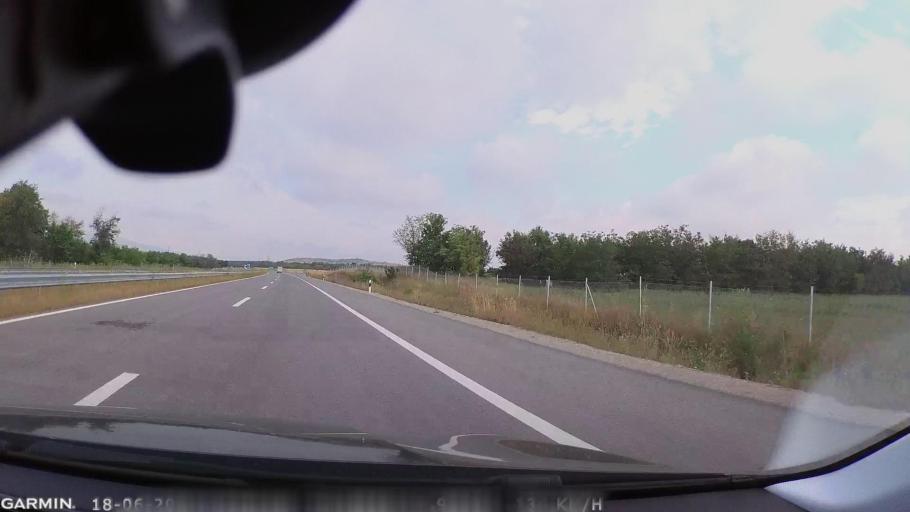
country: MK
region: Sveti Nikole
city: Sveti Nikole
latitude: 41.8397
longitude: 21.9829
